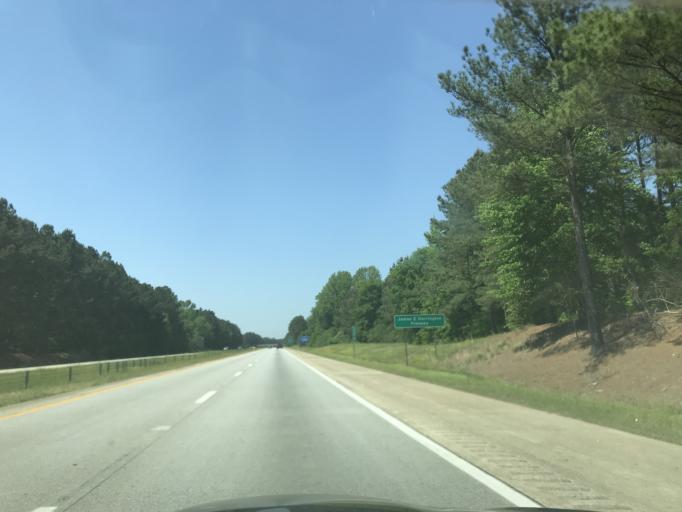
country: US
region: North Carolina
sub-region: Johnston County
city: Benson
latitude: 35.4148
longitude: -78.5260
